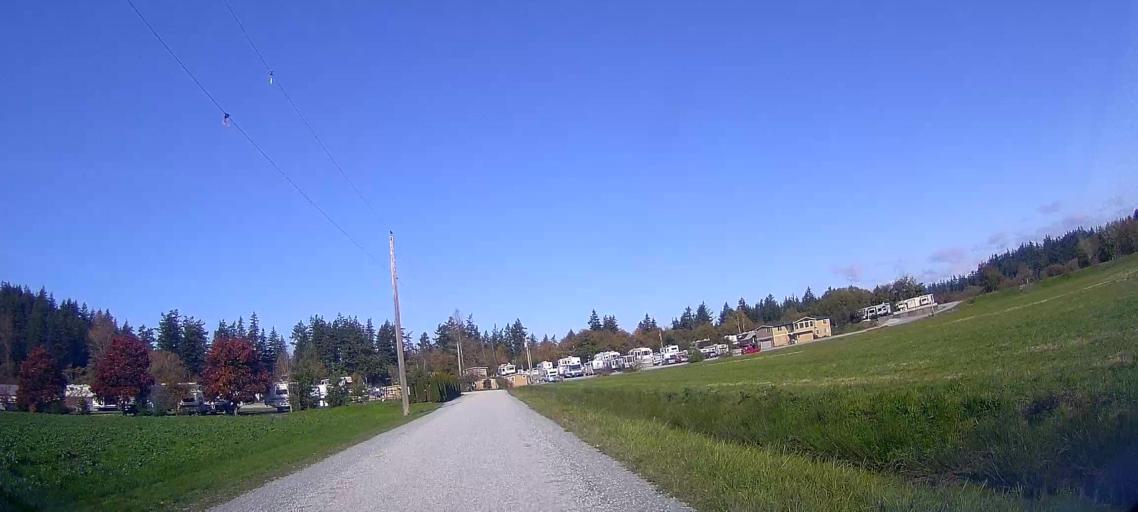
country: US
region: Washington
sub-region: Skagit County
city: Mount Vernon
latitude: 48.3590
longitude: -122.4493
